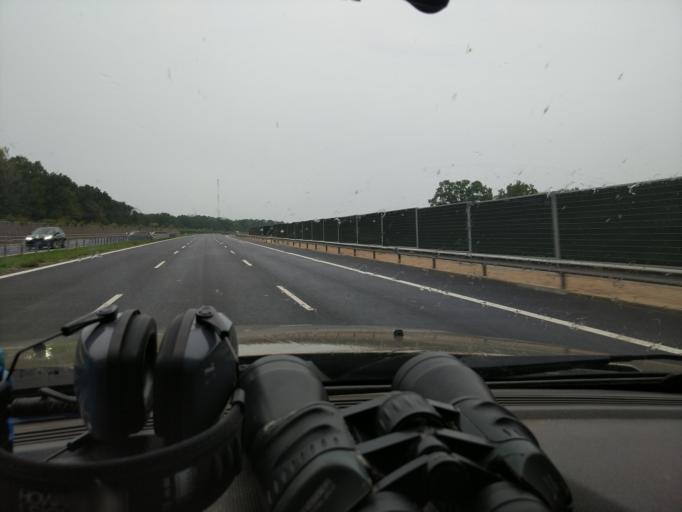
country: PL
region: Masovian Voivodeship
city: Zielonka
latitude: 52.3422
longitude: 21.1564
